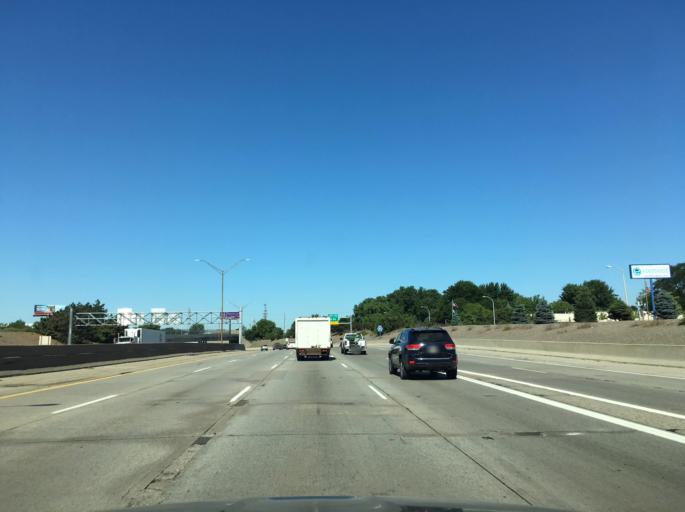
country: US
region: Michigan
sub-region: Macomb County
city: Center Line
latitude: 42.4917
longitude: -83.0328
